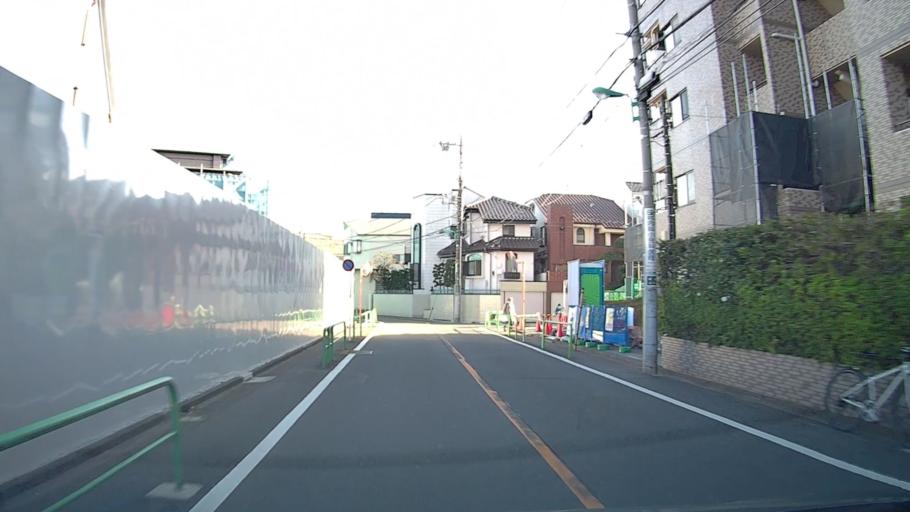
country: JP
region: Saitama
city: Wako
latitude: 35.7503
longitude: 139.6496
